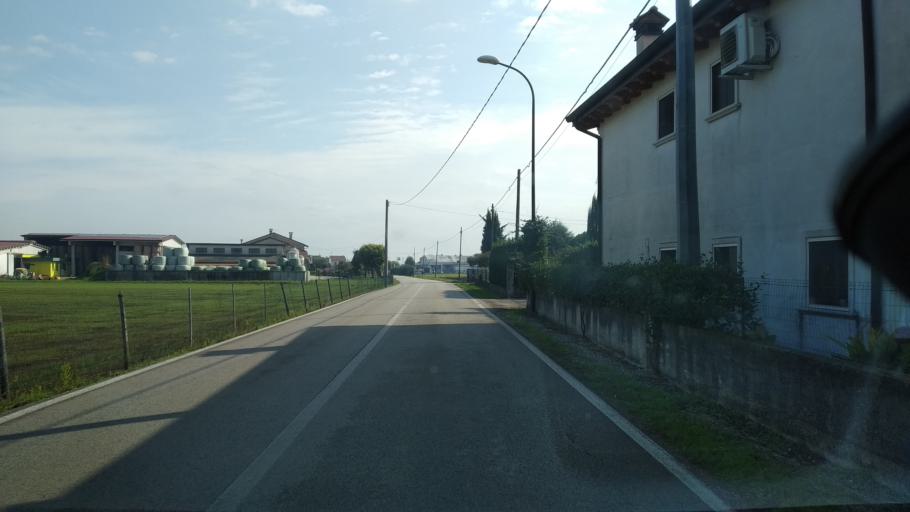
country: IT
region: Veneto
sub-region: Provincia di Vicenza
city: Mason Vicentino
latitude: 45.6951
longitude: 11.6006
